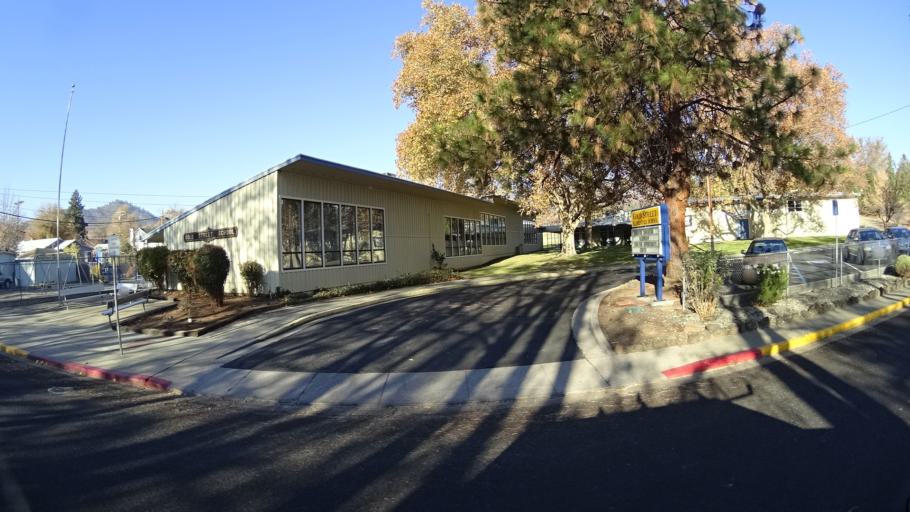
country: US
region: California
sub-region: Siskiyou County
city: Yreka
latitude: 41.7350
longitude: -122.6395
